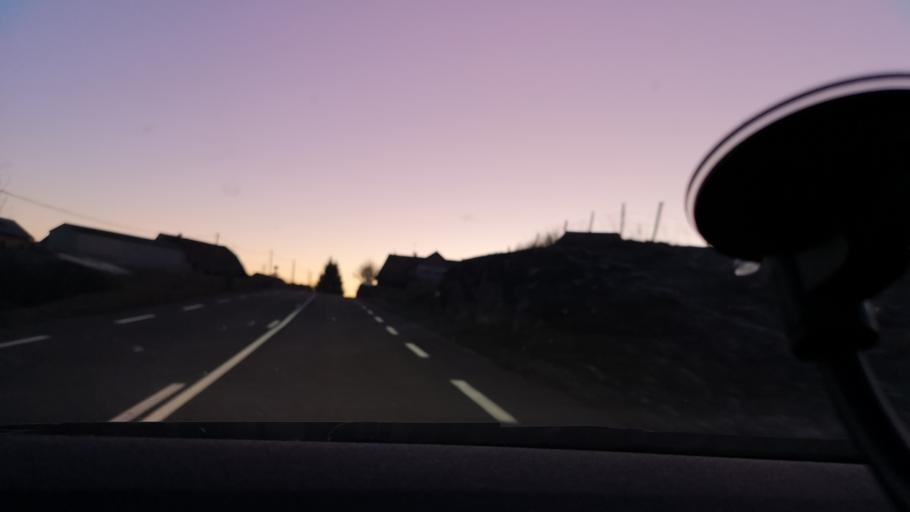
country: FR
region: Franche-Comte
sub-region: Departement du Jura
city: Champagnole
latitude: 46.7976
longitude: 6.0116
